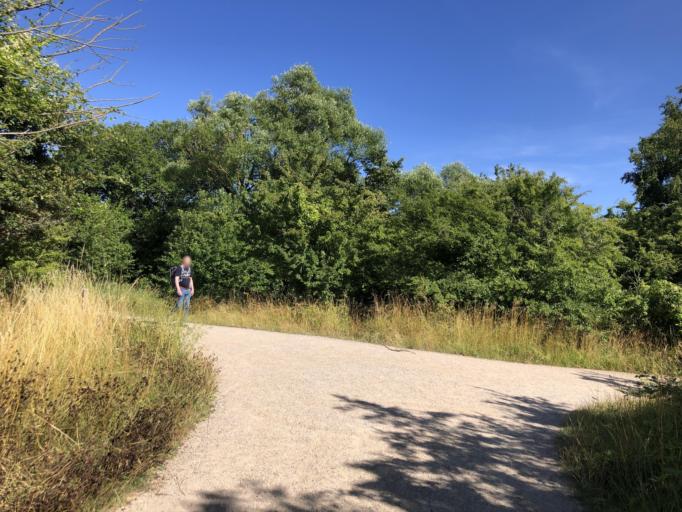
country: DK
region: Capital Region
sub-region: Kobenhavn
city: Copenhagen
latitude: 55.6553
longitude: 12.5786
